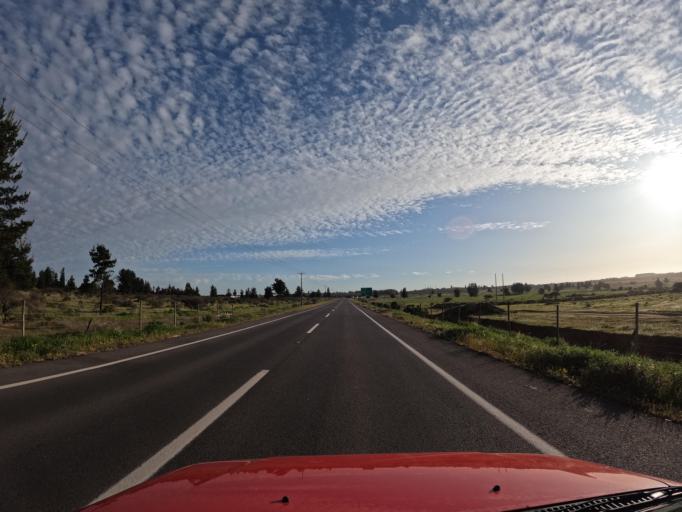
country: CL
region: Valparaiso
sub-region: San Antonio Province
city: San Antonio
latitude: -34.0687
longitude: -71.6288
